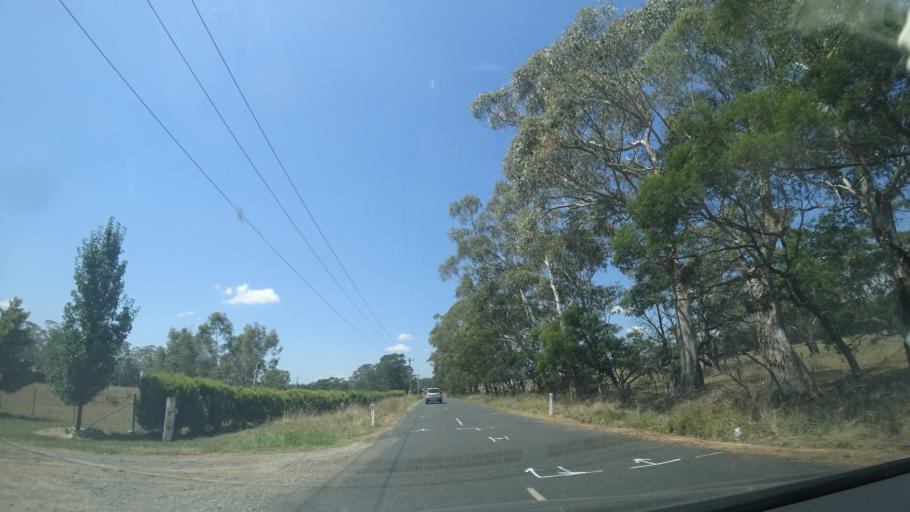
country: AU
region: New South Wales
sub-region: Wingecarribee
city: Bundanoon
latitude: -34.6106
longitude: 150.2630
